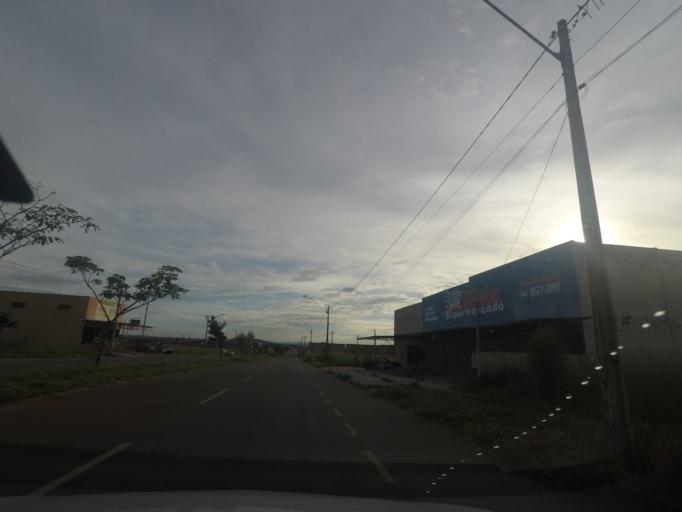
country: BR
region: Goias
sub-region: Trindade
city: Trindade
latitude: -16.7263
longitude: -49.4062
